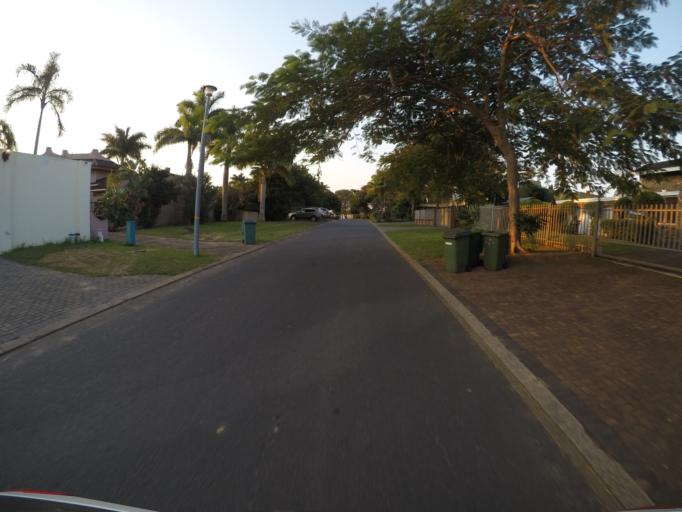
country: ZA
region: KwaZulu-Natal
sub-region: uThungulu District Municipality
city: Richards Bay
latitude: -28.7668
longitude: 32.1198
